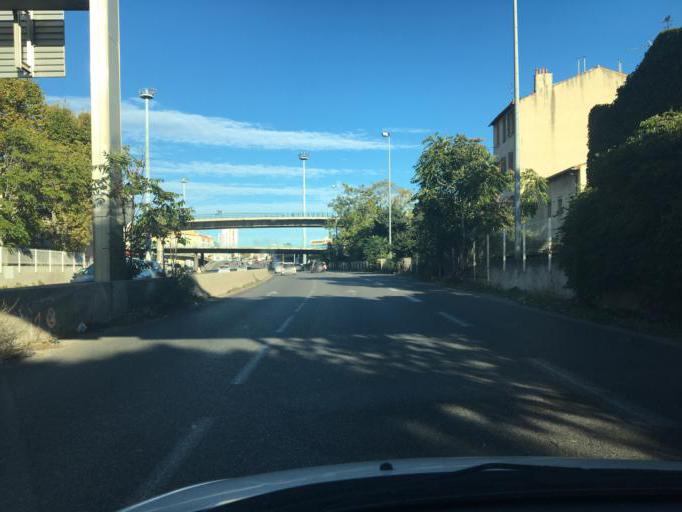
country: FR
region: Provence-Alpes-Cote d'Azur
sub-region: Departement des Bouches-du-Rhone
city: Marseille 05
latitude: 43.2827
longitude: 5.3969
